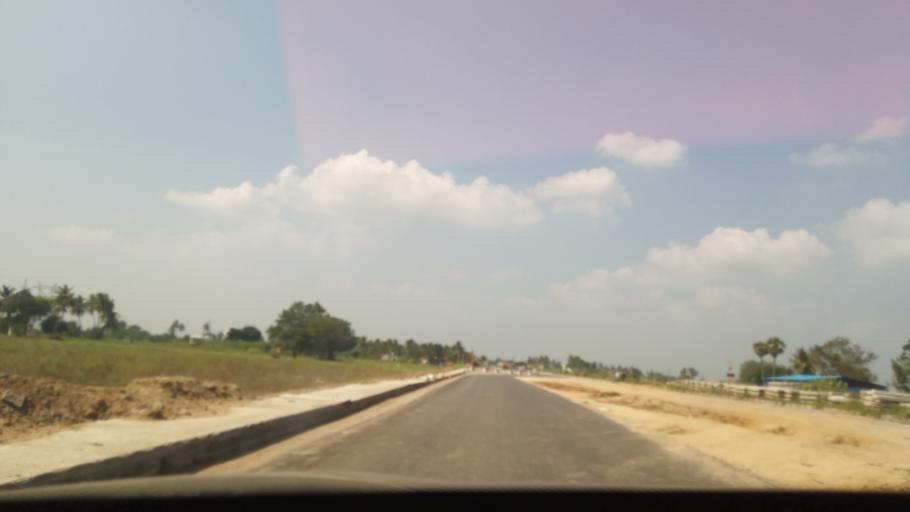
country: IN
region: Tamil Nadu
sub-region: Kancheepuram
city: Kanchipuram
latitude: 12.8969
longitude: 79.5700
